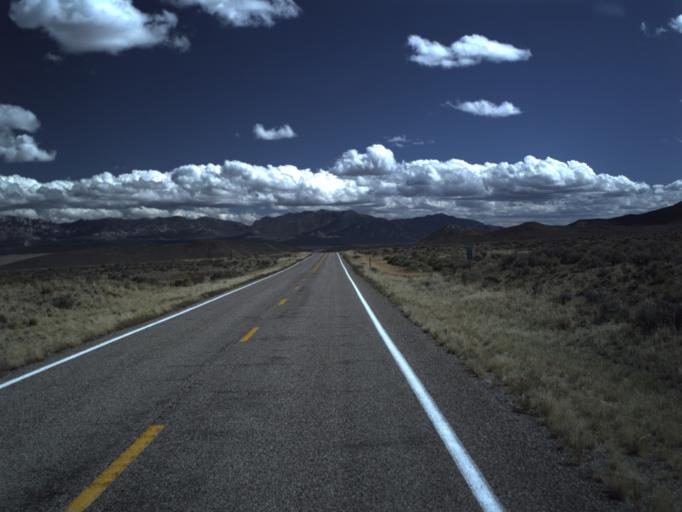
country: US
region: Utah
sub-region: Beaver County
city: Milford
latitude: 38.4319
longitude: -113.1298
